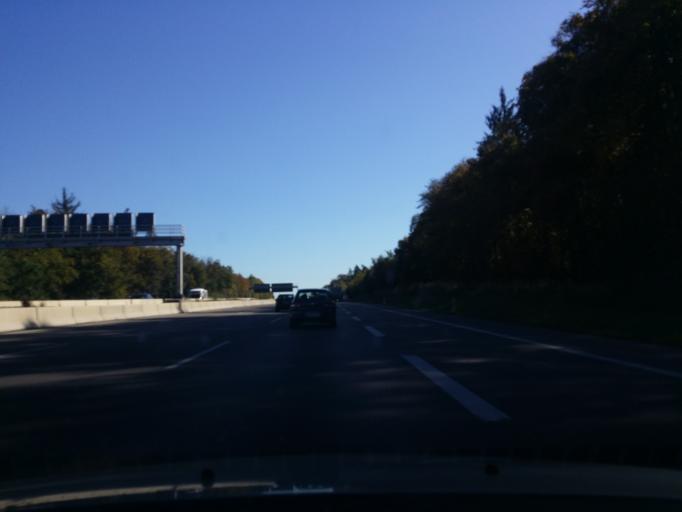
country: DE
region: Baden-Wuerttemberg
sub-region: Regierungsbezirk Stuttgart
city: Schonaich
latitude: 48.7192
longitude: 9.0803
